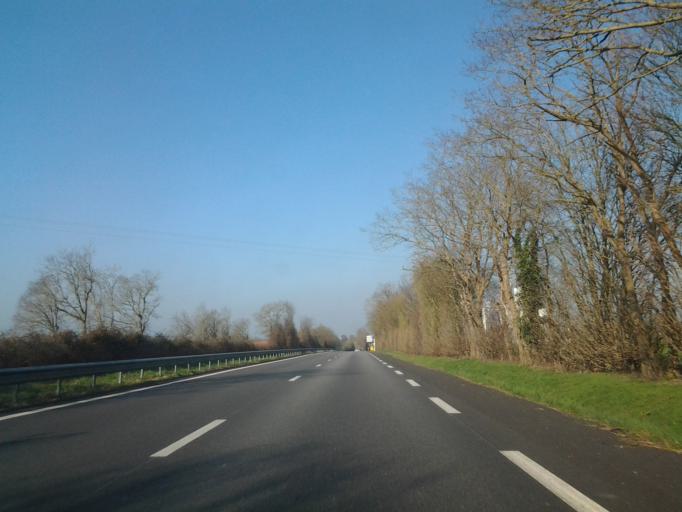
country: FR
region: Pays de la Loire
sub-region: Departement de la Vendee
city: Venansault
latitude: 46.7059
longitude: -1.5104
